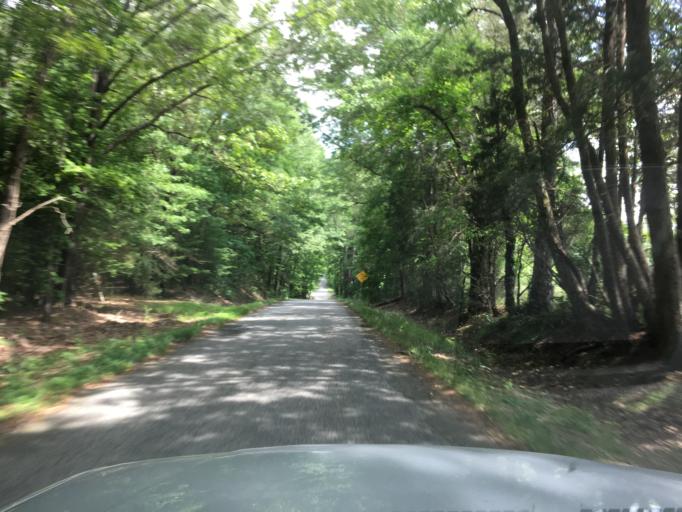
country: US
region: South Carolina
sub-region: Laurens County
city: Watts Mills
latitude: 34.5473
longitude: -81.9437
